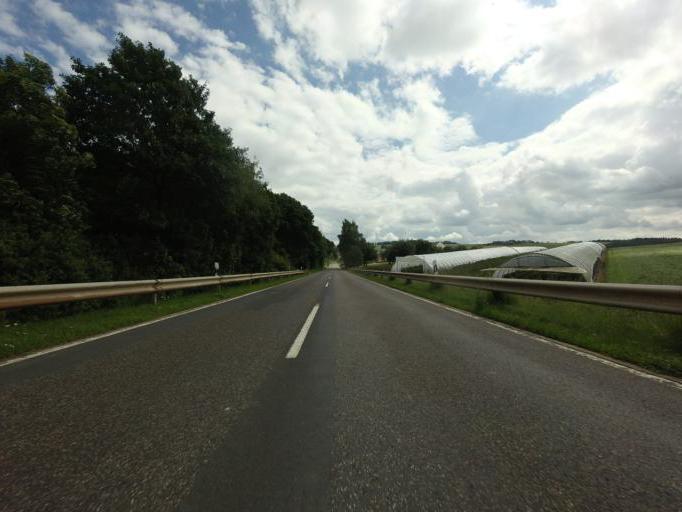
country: DE
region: Rheinland-Pfalz
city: Dungenheim
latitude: 50.2817
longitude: 7.1540
